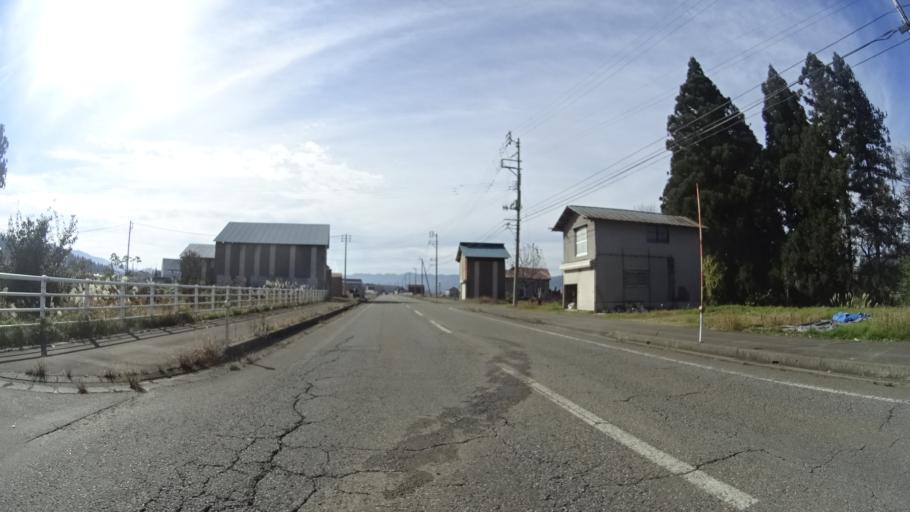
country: JP
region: Niigata
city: Muikamachi
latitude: 37.1795
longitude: 138.9750
